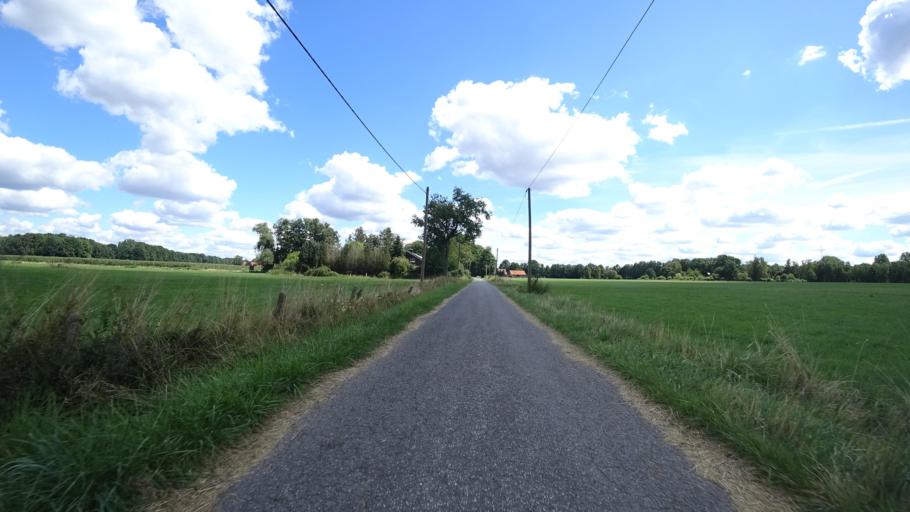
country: DE
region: North Rhine-Westphalia
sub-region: Regierungsbezirk Detmold
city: Guetersloh
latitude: 51.9372
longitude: 8.3926
